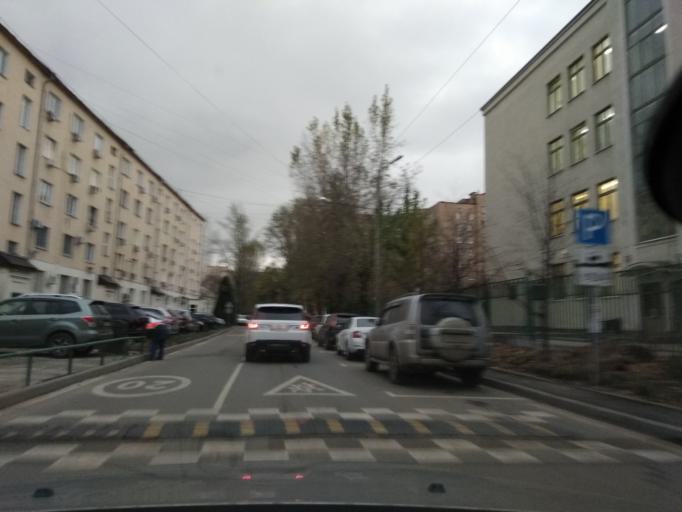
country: RU
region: Moscow
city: Mar'ina Roshcha
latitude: 55.7958
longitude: 37.6012
